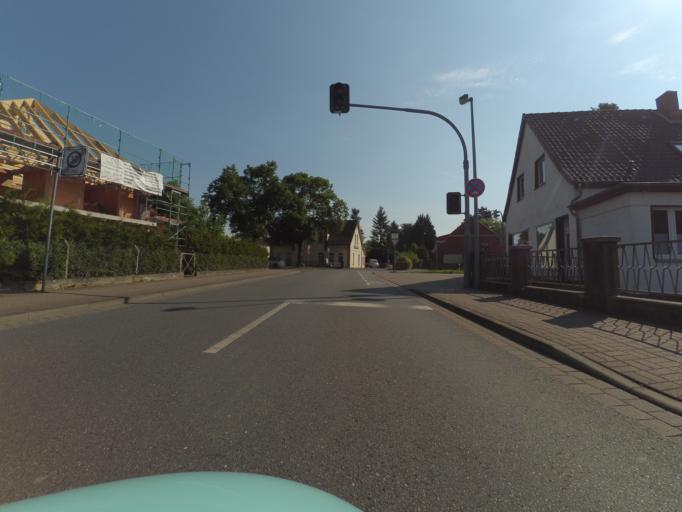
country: DE
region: Lower Saxony
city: Burgdorf
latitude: 52.4408
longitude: 10.0134
